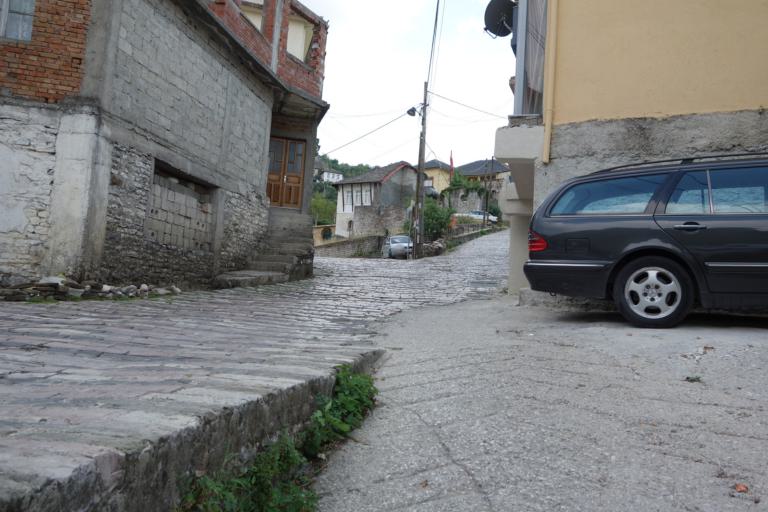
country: AL
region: Gjirokaster
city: Gjirokaster
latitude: 40.0714
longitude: 20.1373
